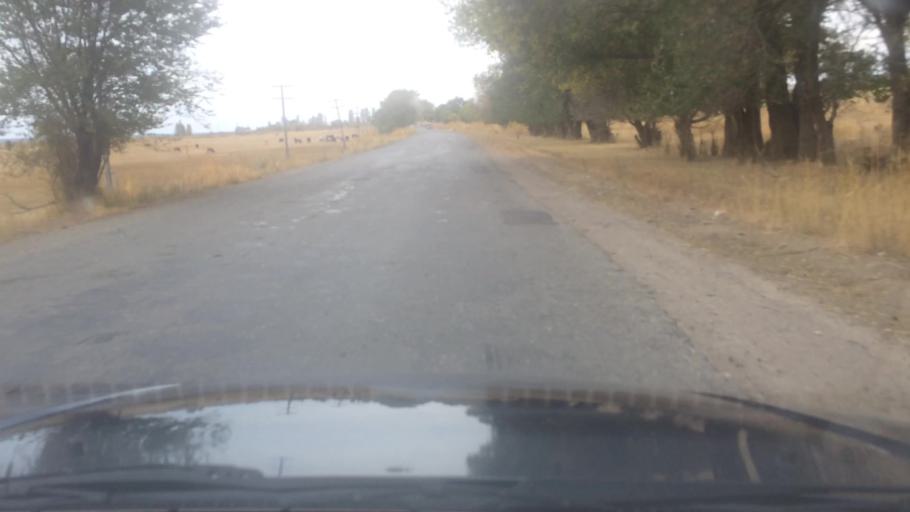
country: KG
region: Ysyk-Koel
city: Balykchy
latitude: 42.3080
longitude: 76.4656
